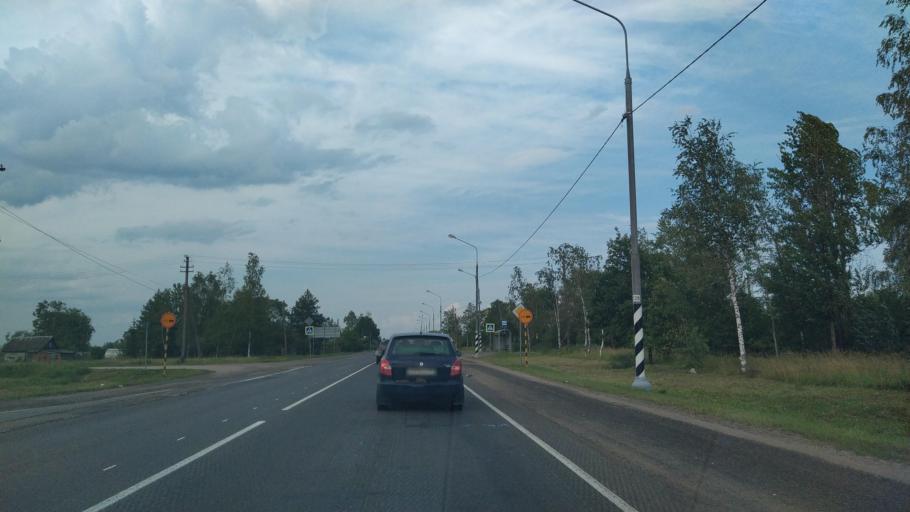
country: RU
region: Novgorod
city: Pankovka
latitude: 58.3859
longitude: 31.0222
